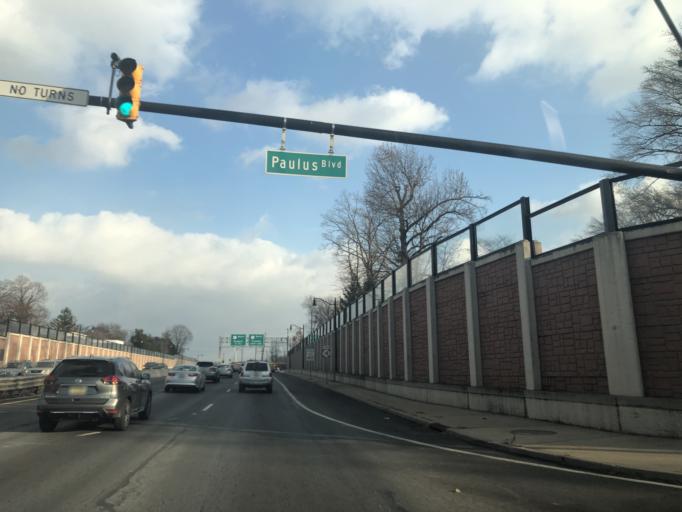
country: US
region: New Jersey
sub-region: Middlesex County
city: Highland Park
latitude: 40.4853
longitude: -74.4230
